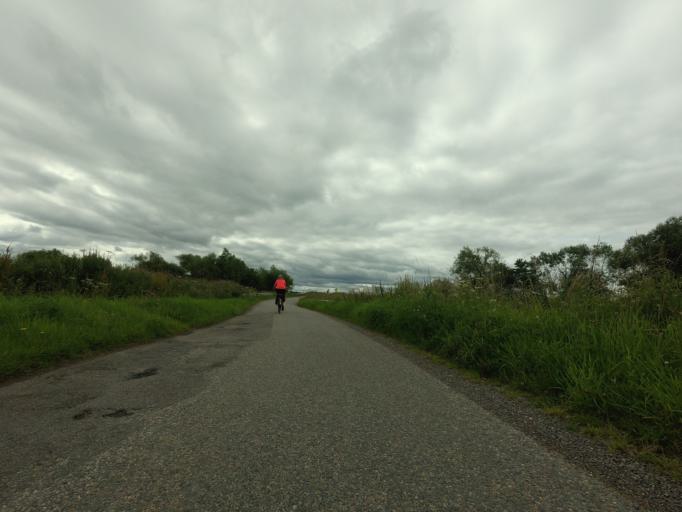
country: GB
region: Scotland
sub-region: Moray
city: Forres
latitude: 57.6254
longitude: -3.6070
